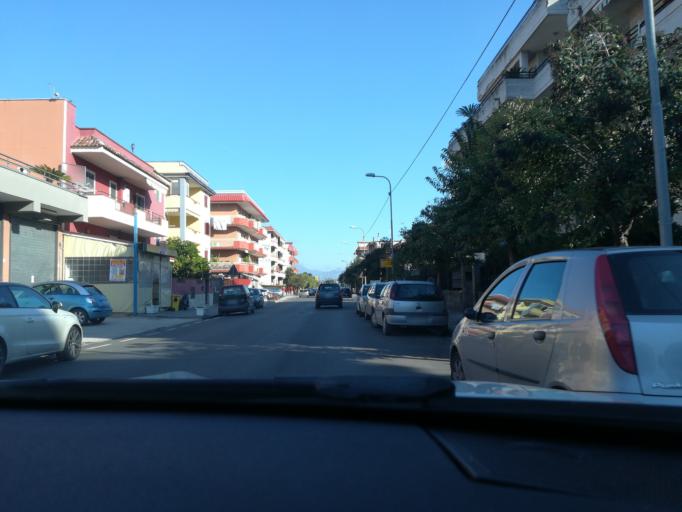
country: IT
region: Campania
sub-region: Provincia di Napoli
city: Sant'Anastasia
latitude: 40.8727
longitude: 14.3984
